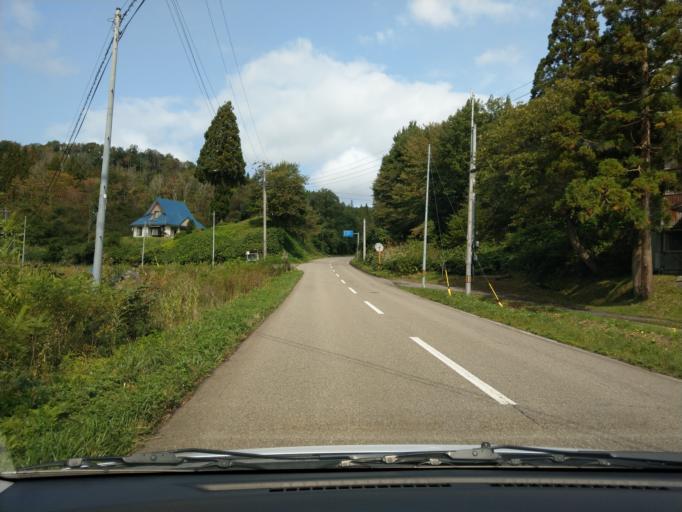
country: JP
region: Akita
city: Omagari
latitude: 39.4816
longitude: 140.3120
